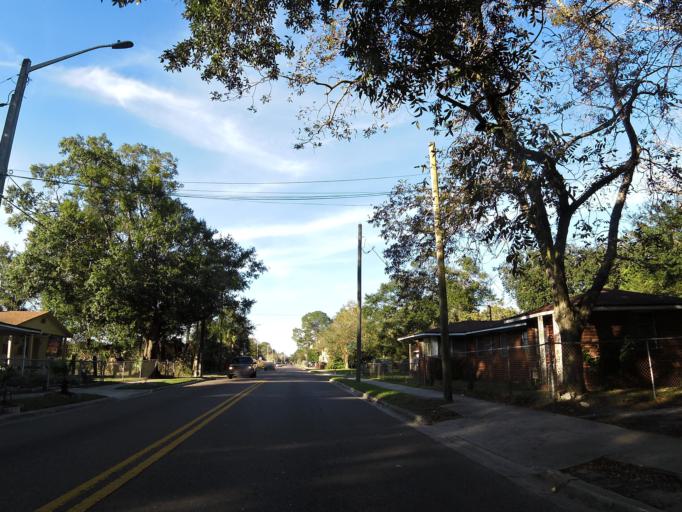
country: US
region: Florida
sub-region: Duval County
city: Jacksonville
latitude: 30.3516
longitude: -81.6863
